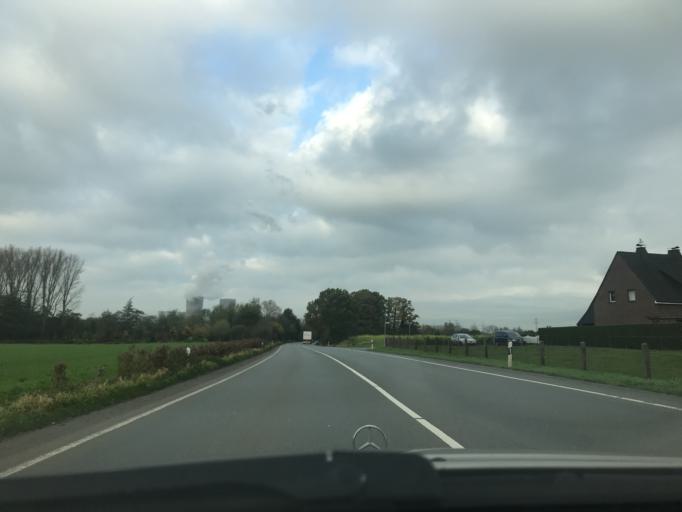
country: DE
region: North Rhine-Westphalia
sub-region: Regierungsbezirk Arnsberg
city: Welver
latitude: 51.6735
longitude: 8.0129
